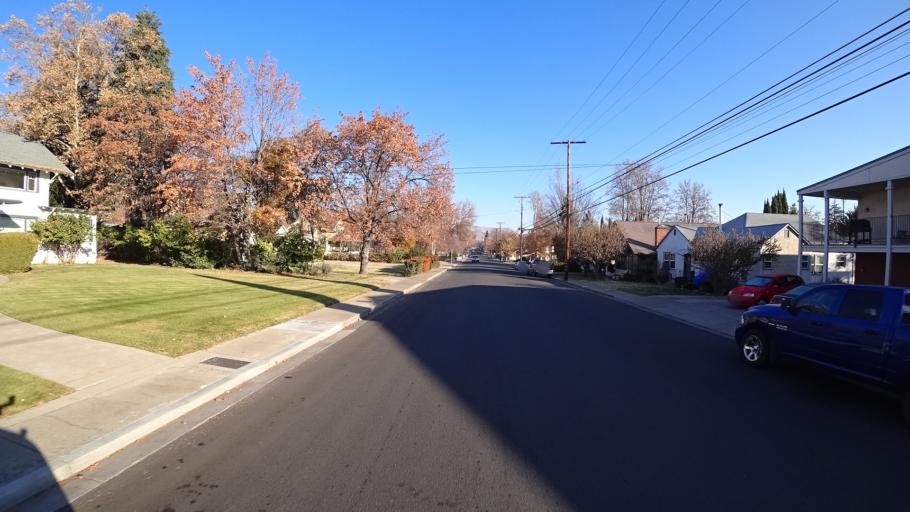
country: US
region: California
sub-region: Siskiyou County
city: Yreka
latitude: 41.7341
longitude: -122.6377
